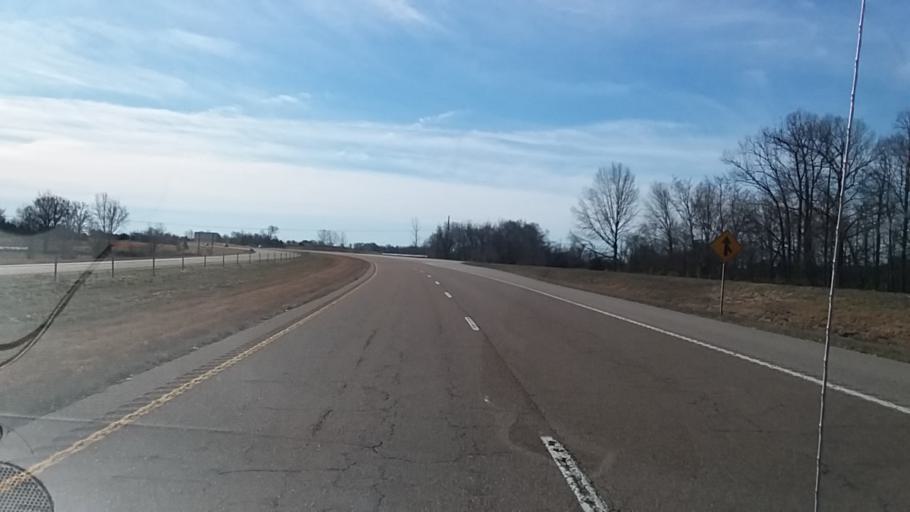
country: US
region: Tennessee
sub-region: Crockett County
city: Alamo
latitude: 35.7938
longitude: -89.1586
